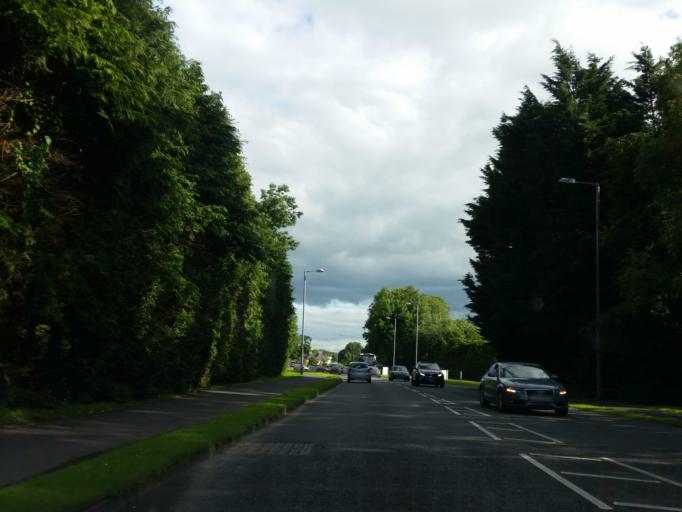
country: GB
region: Northern Ireland
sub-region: Fermanagh District
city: Enniskillen
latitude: 54.3374
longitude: -7.6249
